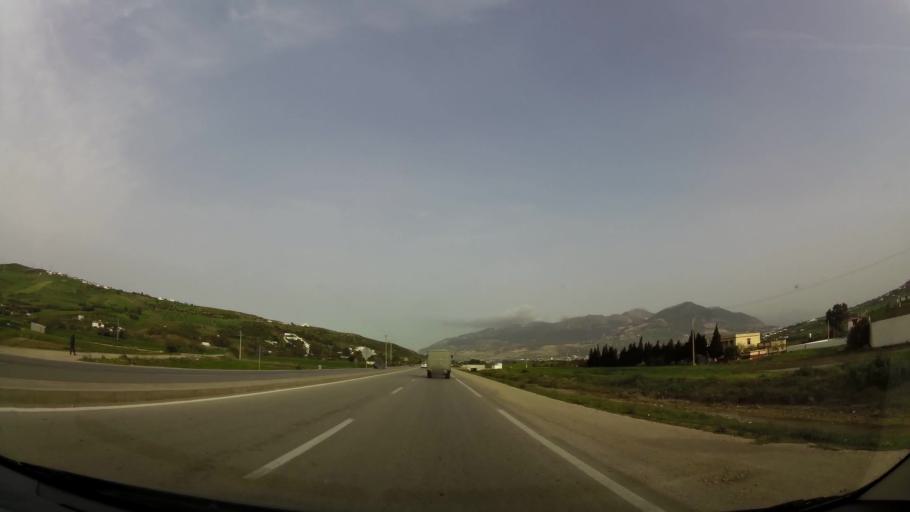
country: MA
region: Tanger-Tetouan
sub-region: Tetouan
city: Saddina
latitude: 35.5599
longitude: -5.4659
